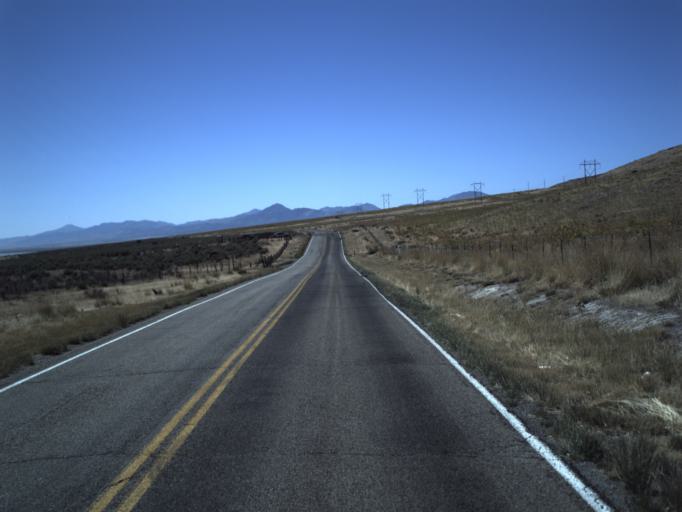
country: US
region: Utah
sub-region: Utah County
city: Saratoga Springs
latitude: 40.2006
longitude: -111.9002
